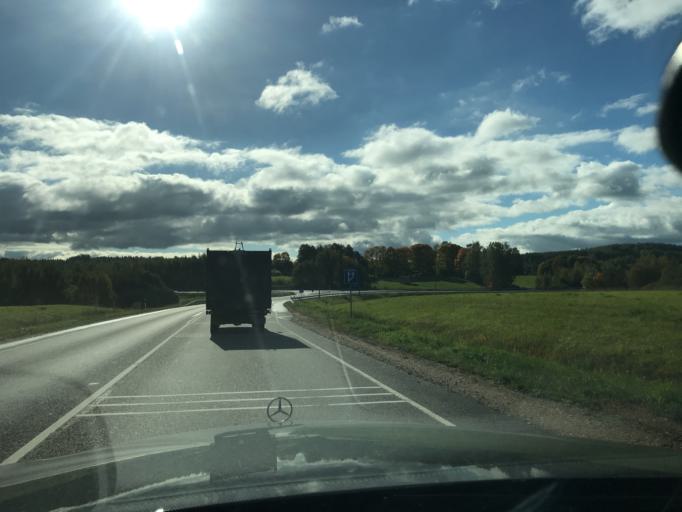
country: EE
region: Vorumaa
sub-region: Voru linn
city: Voru
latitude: 57.8121
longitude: 27.0650
